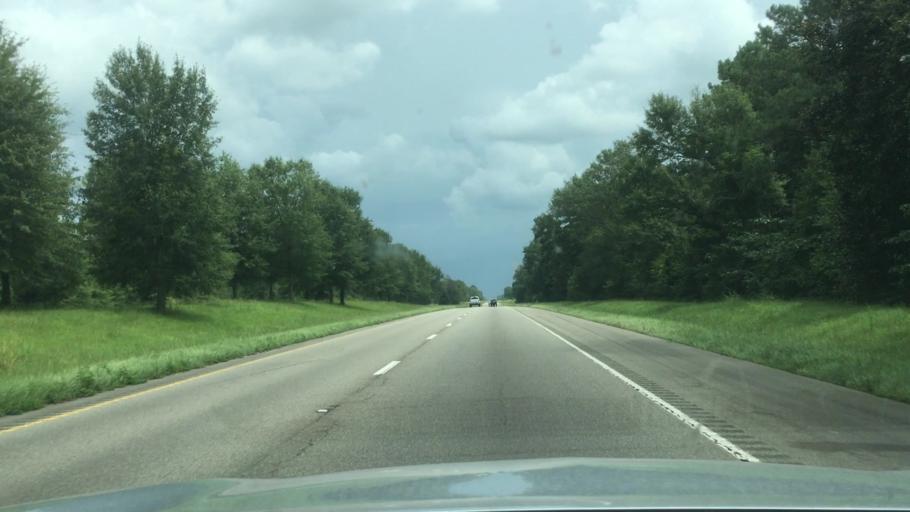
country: US
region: Mississippi
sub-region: Pearl River County
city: Carriere
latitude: 30.5725
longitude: -89.6334
